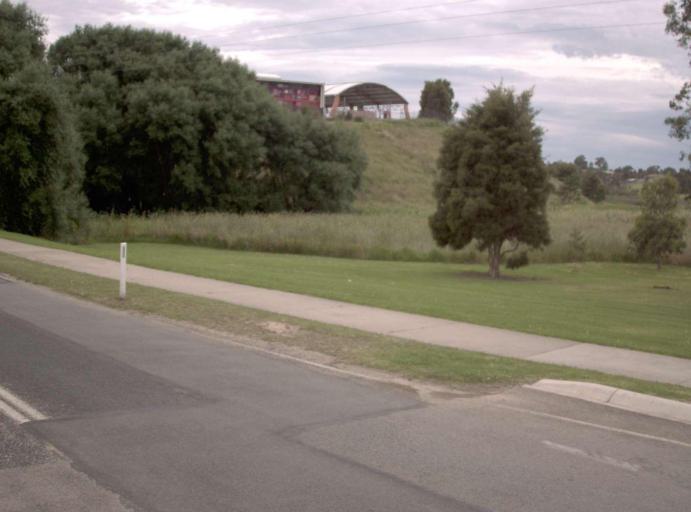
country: AU
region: Victoria
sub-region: East Gippsland
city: Bairnsdale
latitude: -37.8111
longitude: 147.6188
